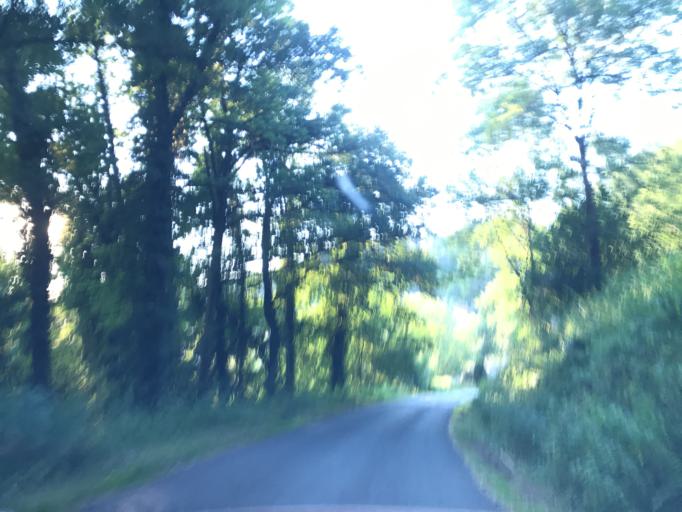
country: FR
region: Auvergne
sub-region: Departement du Puy-de-Dome
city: Courpiere
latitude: 45.7535
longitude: 3.6200
